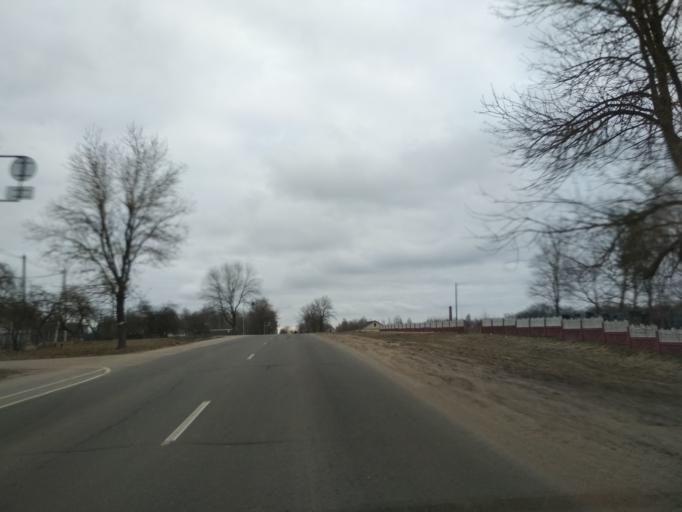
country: BY
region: Minsk
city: Svislach
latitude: 53.5715
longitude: 27.9549
